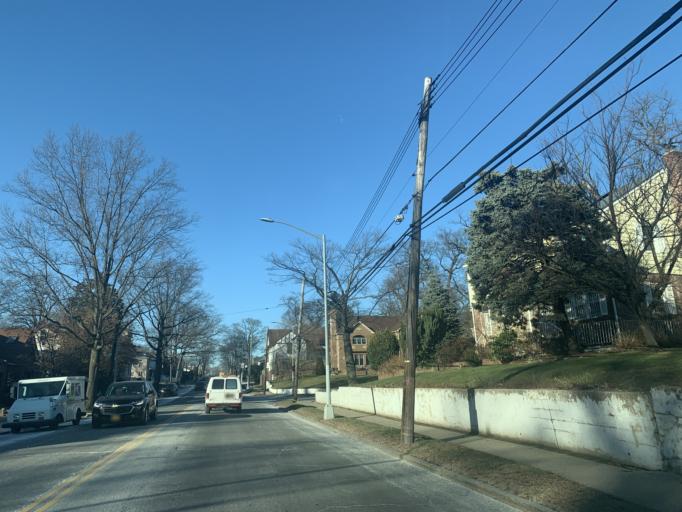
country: US
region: New York
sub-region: Queens County
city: Jamaica
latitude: 40.7180
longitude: -73.7749
